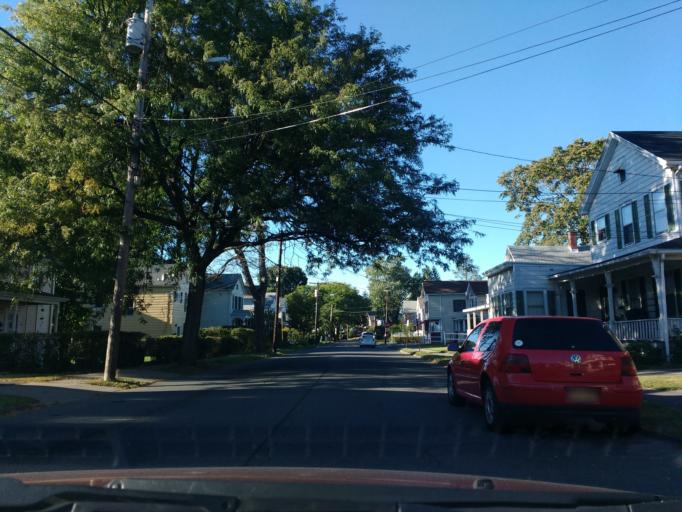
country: US
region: New York
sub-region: Ulster County
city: Kingston
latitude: 41.9290
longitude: -73.9946
